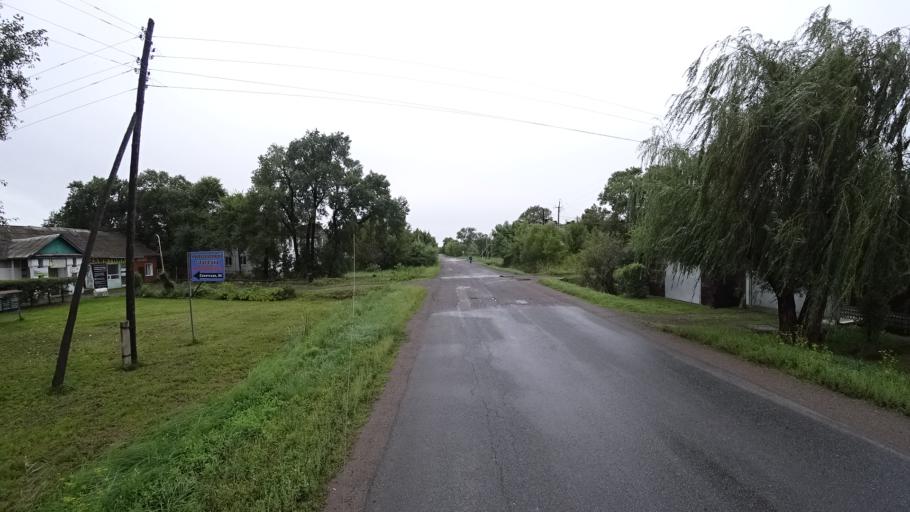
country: RU
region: Primorskiy
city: Chernigovka
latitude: 44.3393
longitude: 132.5733
